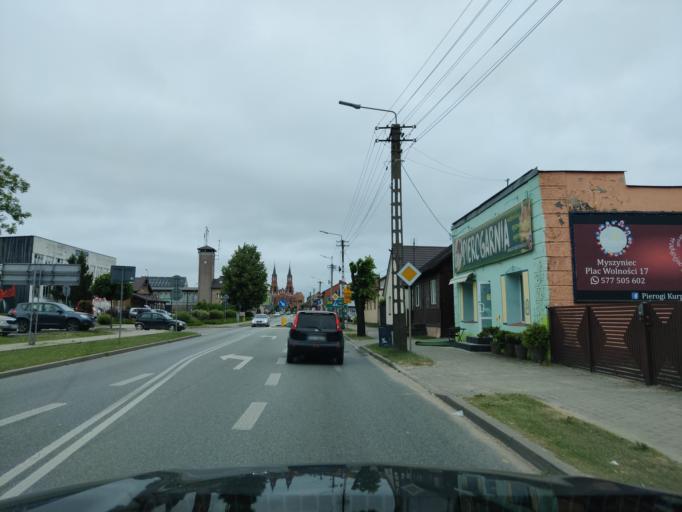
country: PL
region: Masovian Voivodeship
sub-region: Powiat ostrolecki
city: Myszyniec
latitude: 53.3850
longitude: 21.3396
